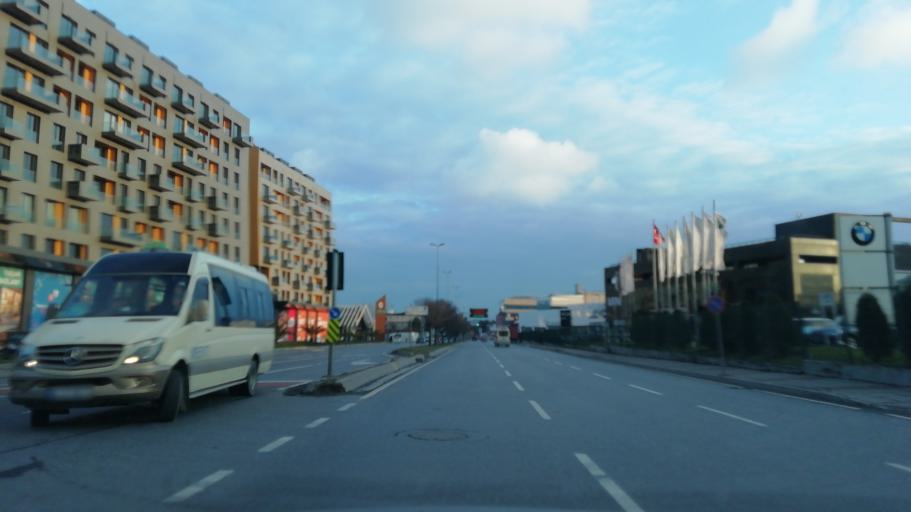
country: TR
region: Istanbul
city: Yakuplu
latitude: 40.9927
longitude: 28.7174
